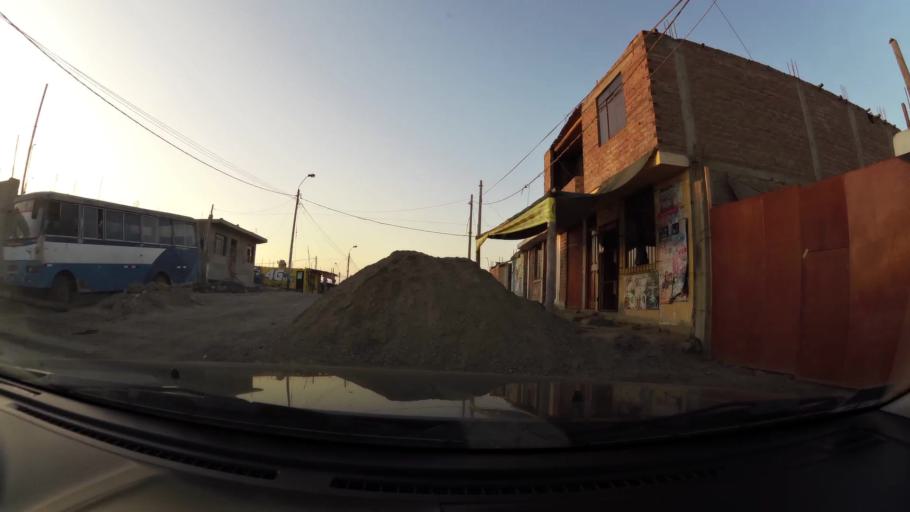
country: PE
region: Ica
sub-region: Provincia de Pisco
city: San Clemente
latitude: -13.6763
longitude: -76.1547
